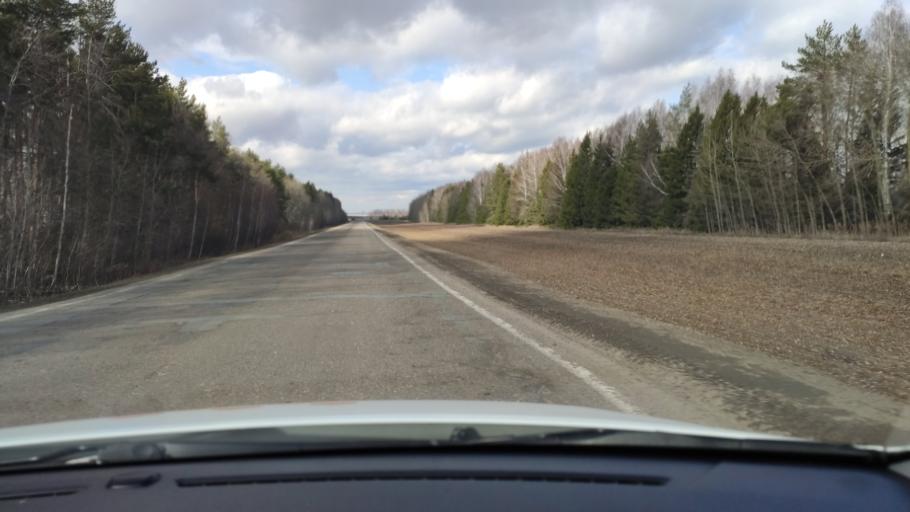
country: RU
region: Tatarstan
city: Vysokaya Gora
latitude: 56.1068
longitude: 49.1782
